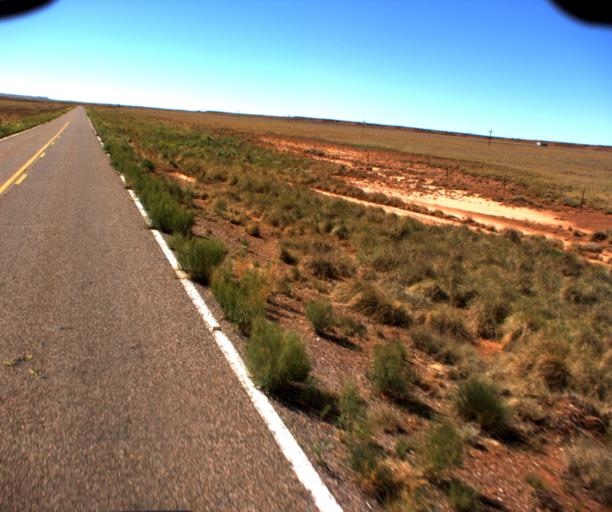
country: US
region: Arizona
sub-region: Coconino County
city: LeChee
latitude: 35.1697
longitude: -110.9167
